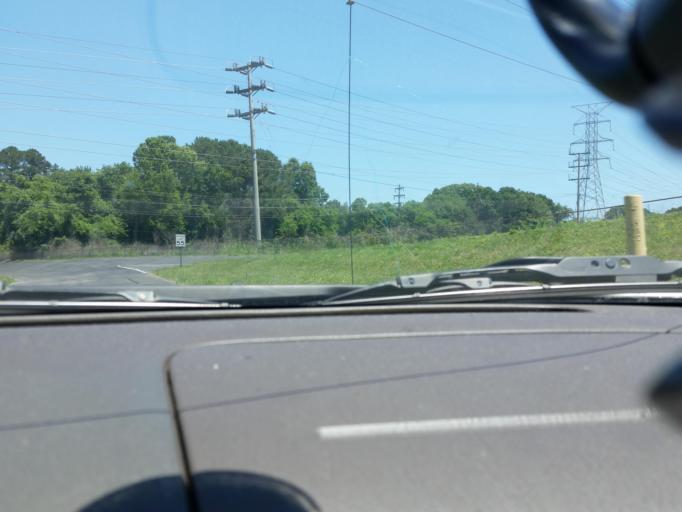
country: US
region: Tennessee
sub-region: Hamilton County
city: East Chattanooga
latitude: 35.0959
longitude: -85.2306
